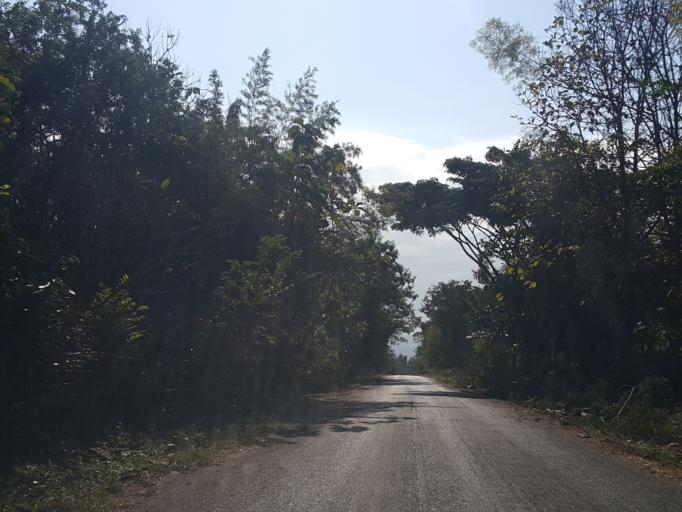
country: TH
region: Lampang
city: Mae Mo
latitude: 18.2976
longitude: 99.6681
